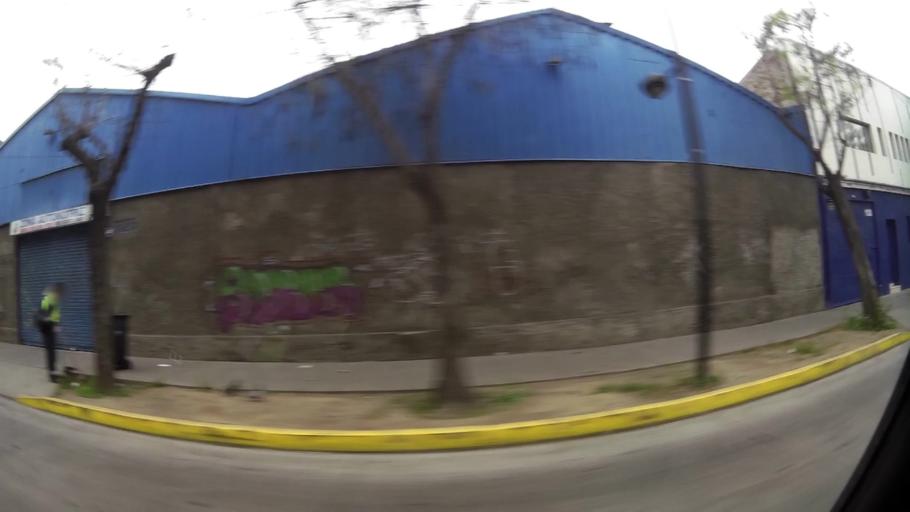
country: CL
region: Santiago Metropolitan
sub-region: Provincia de Santiago
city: Santiago
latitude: -33.4597
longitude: -70.6450
